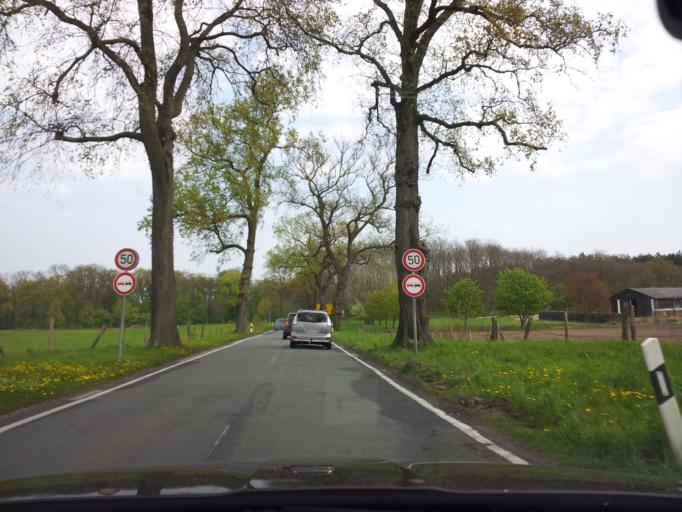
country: DE
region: Brandenburg
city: Muncheberg
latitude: 52.5061
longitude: 14.2264
